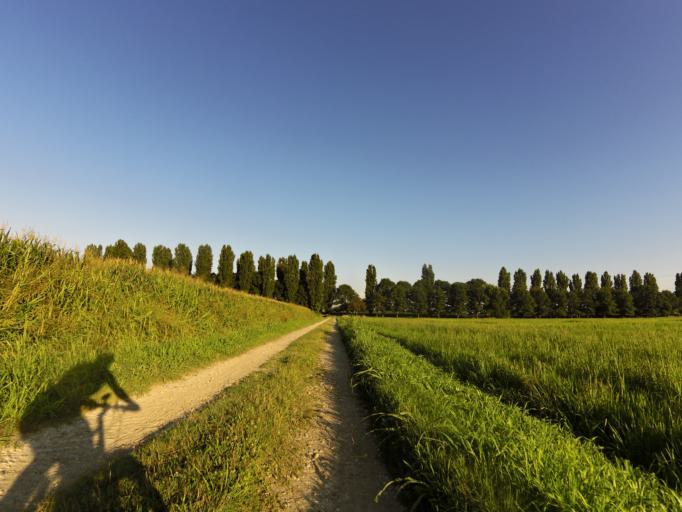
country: IT
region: Lombardy
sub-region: Citta metropolitana di Milano
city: San Giuliano Milanese
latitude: 45.3896
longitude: 9.2808
